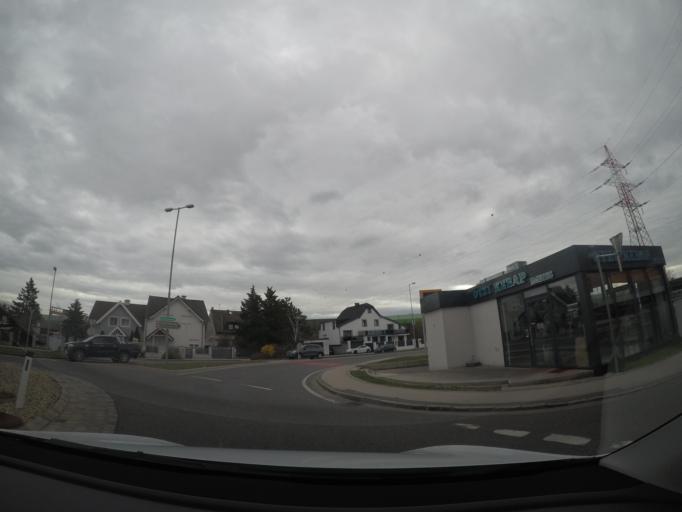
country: AT
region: Lower Austria
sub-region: Politischer Bezirk Modling
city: Vosendorf
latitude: 48.1293
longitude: 16.3268
